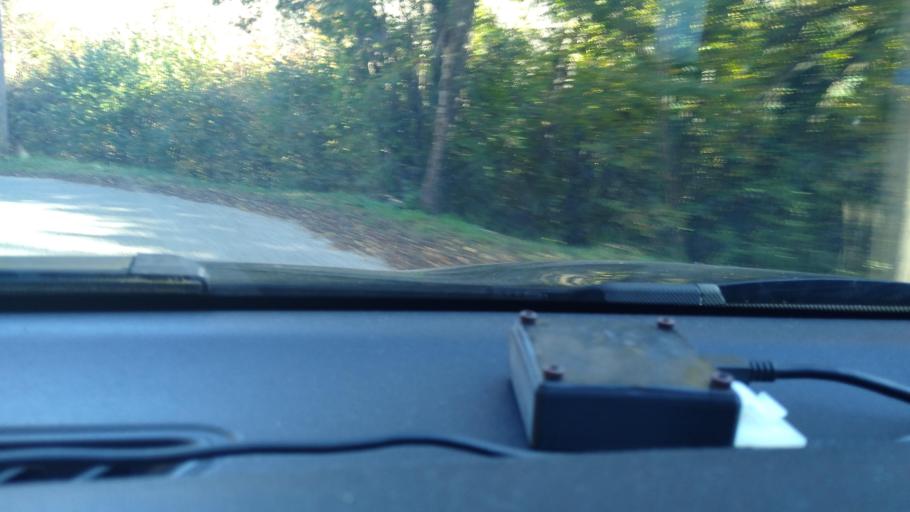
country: FR
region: Languedoc-Roussillon
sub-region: Departement de l'Aude
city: Quillan
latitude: 42.7331
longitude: 2.0814
